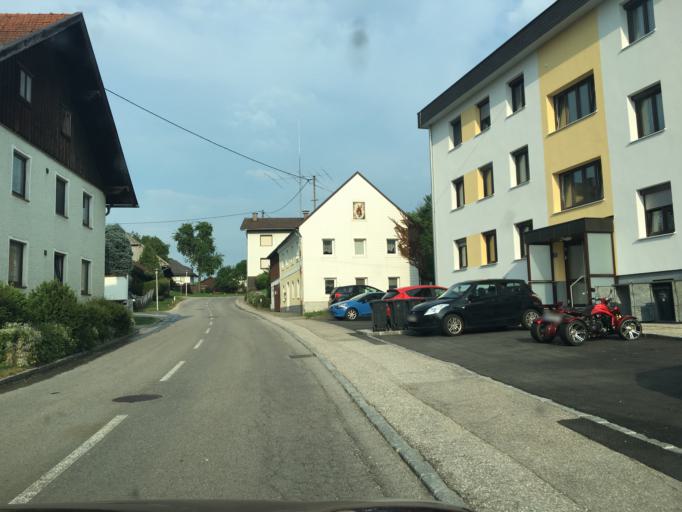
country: AT
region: Upper Austria
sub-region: Politischer Bezirk Ried im Innkreis
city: Waldzell
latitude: 48.1355
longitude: 13.4291
